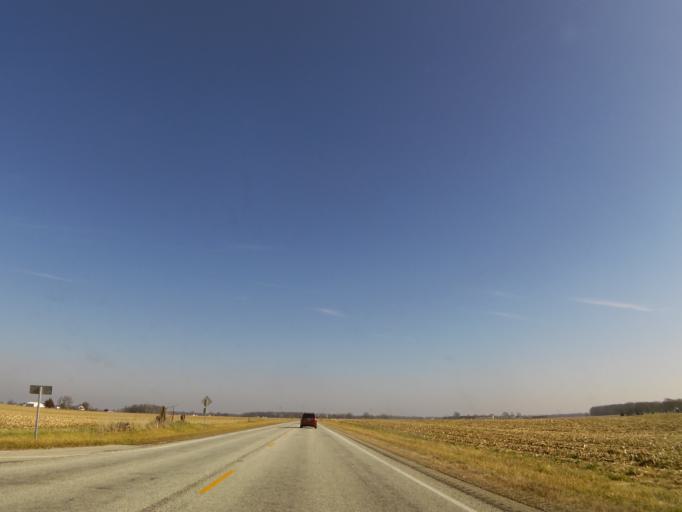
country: US
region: Indiana
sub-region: Shelby County
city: Morristown
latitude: 39.5707
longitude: -85.6169
